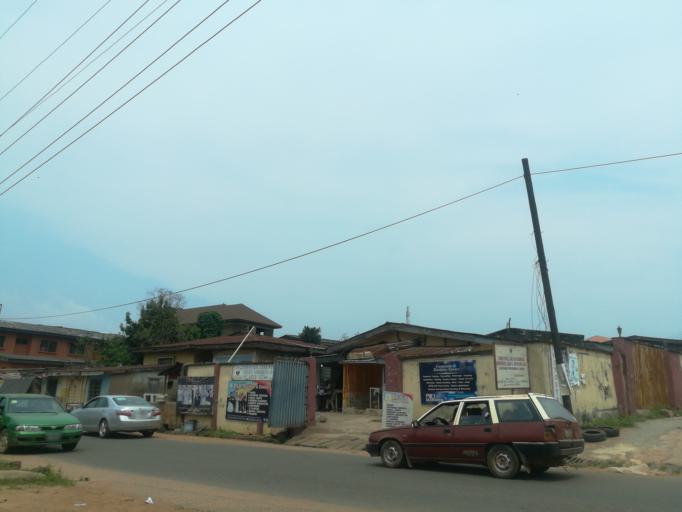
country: NG
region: Oyo
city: Ibadan
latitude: 7.4259
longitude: 3.9332
